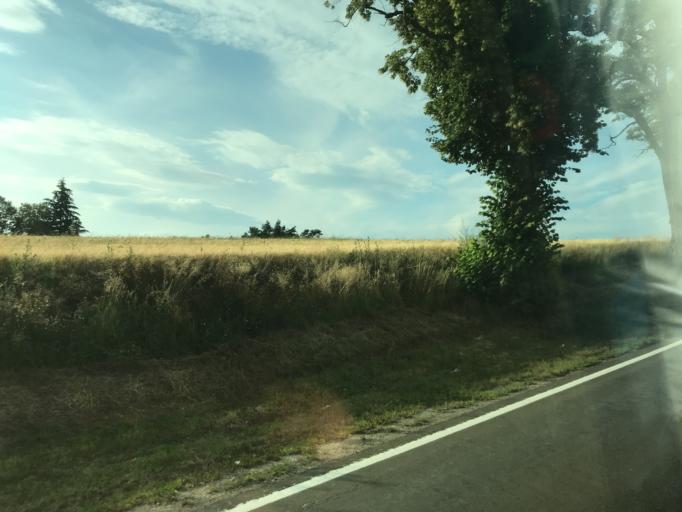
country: CZ
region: Jihocesky
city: Rudolfov
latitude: 49.0014
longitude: 14.5525
